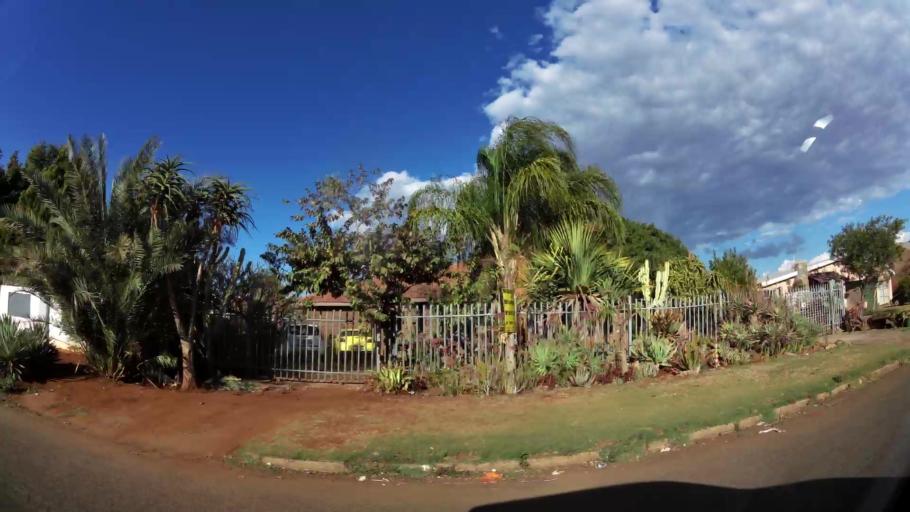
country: ZA
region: Limpopo
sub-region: Waterberg District Municipality
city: Mokopane
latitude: -24.1888
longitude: 28.9976
